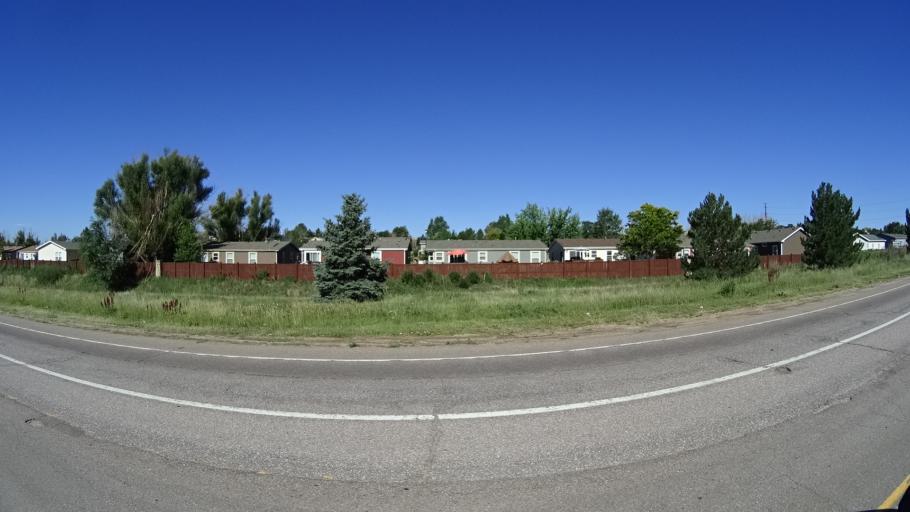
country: US
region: Colorado
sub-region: El Paso County
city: Cimarron Hills
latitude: 38.8978
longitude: -104.6829
